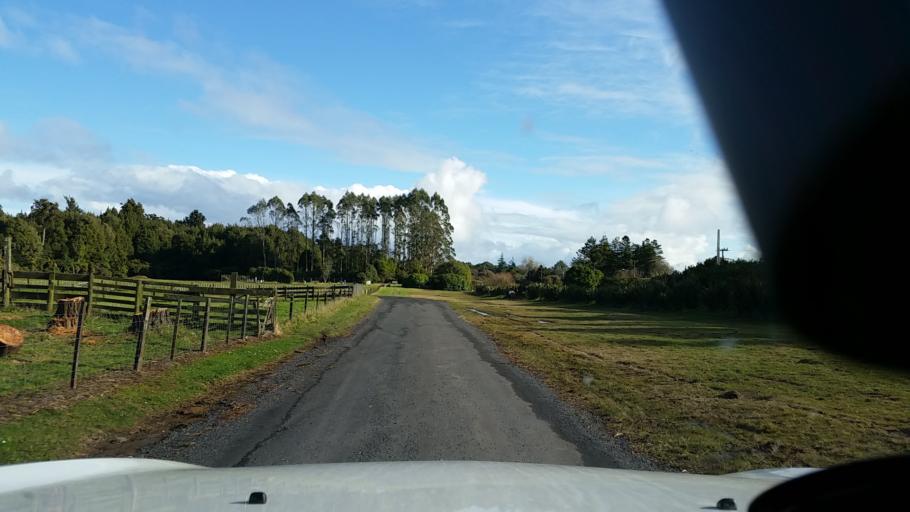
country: NZ
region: Bay of Plenty
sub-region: Rotorua District
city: Rotorua
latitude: -38.0977
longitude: 176.0747
